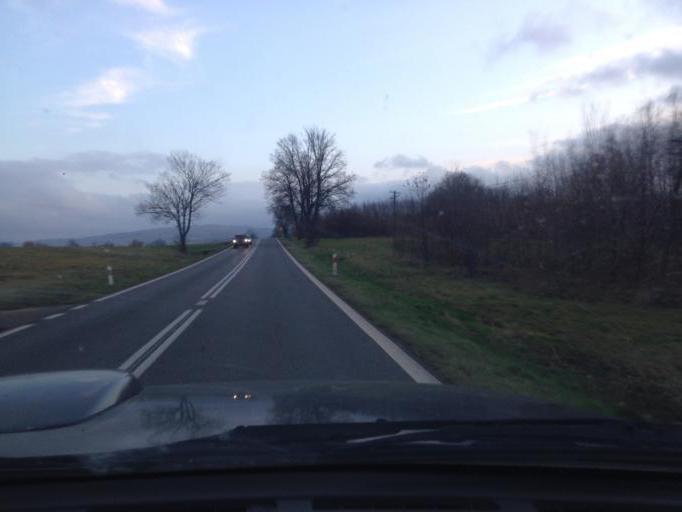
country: PL
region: Subcarpathian Voivodeship
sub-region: Powiat jasielski
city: Nowy Zmigrod
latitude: 49.6276
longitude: 21.5330
